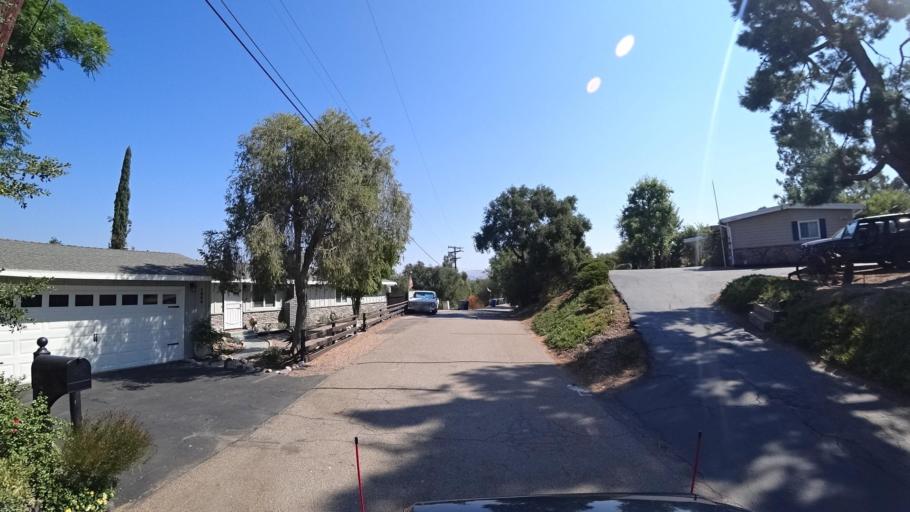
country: US
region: California
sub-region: San Diego County
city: Fallbrook
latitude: 33.3916
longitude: -117.2244
